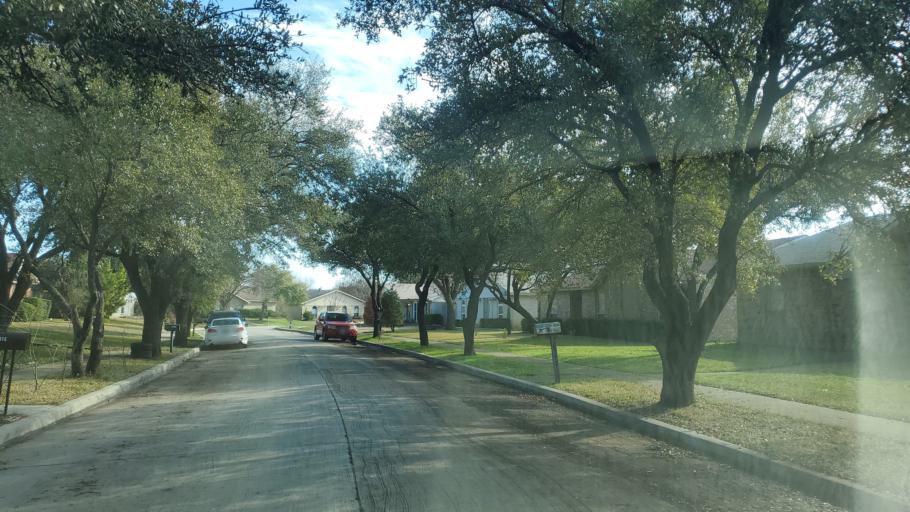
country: US
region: Texas
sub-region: Dallas County
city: Carrollton
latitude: 32.9951
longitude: -96.8758
